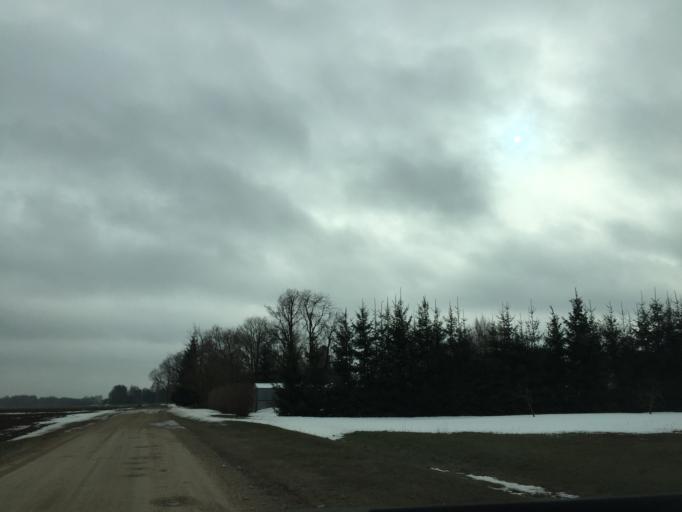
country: LV
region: Rundales
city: Pilsrundale
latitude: 56.5286
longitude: 23.9886
